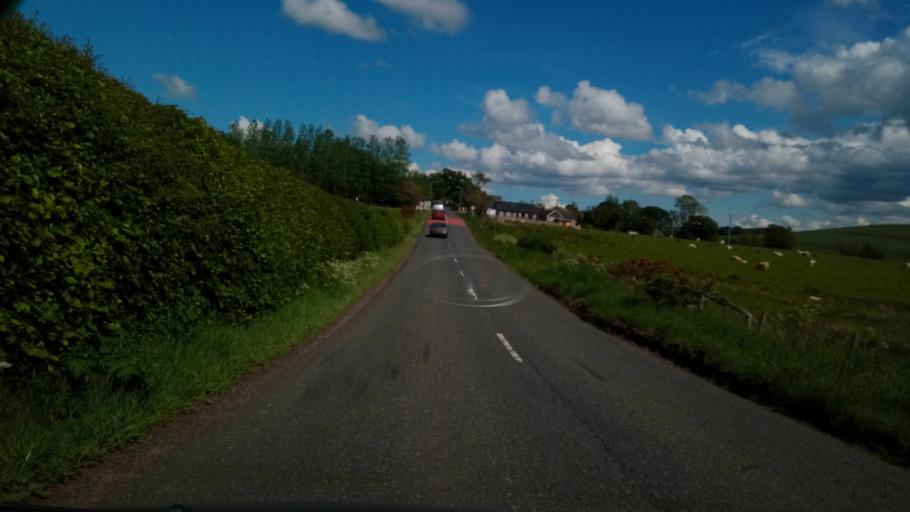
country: GB
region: Scotland
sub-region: The Scottish Borders
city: Jedburgh
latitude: 55.3880
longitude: -2.5995
